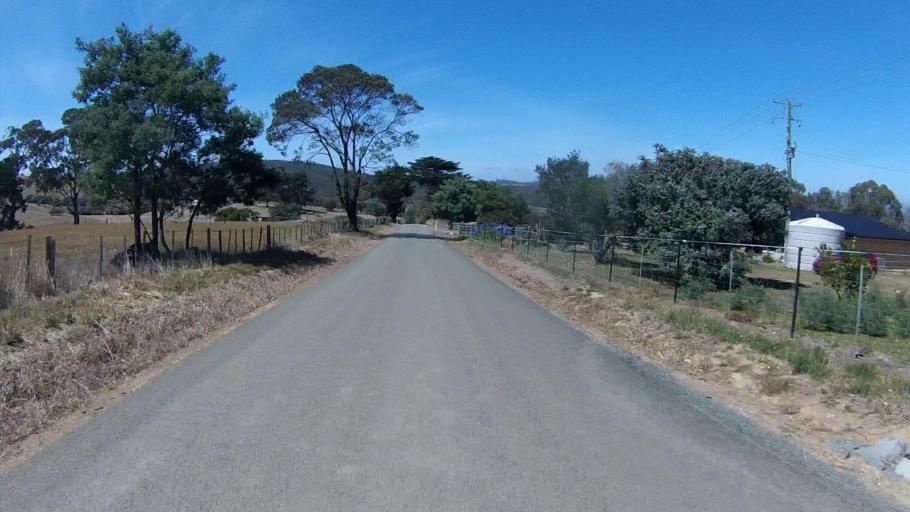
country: AU
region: Tasmania
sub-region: Sorell
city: Sorell
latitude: -42.7941
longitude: 147.6397
